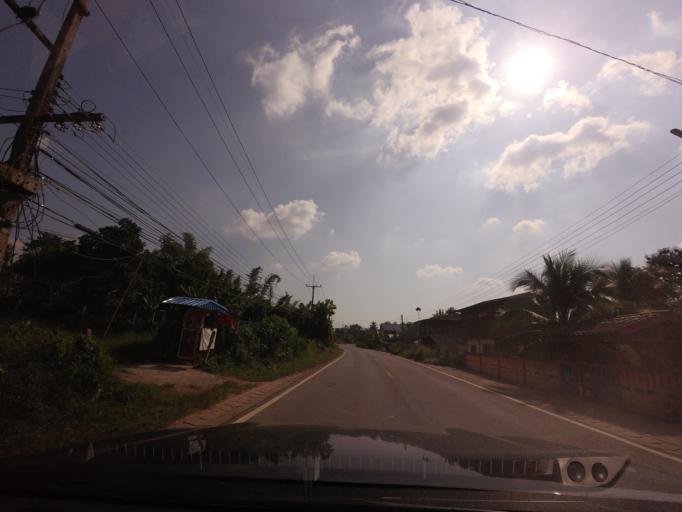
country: TH
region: Nan
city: Santi Suk
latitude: 18.9561
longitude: 100.9231
